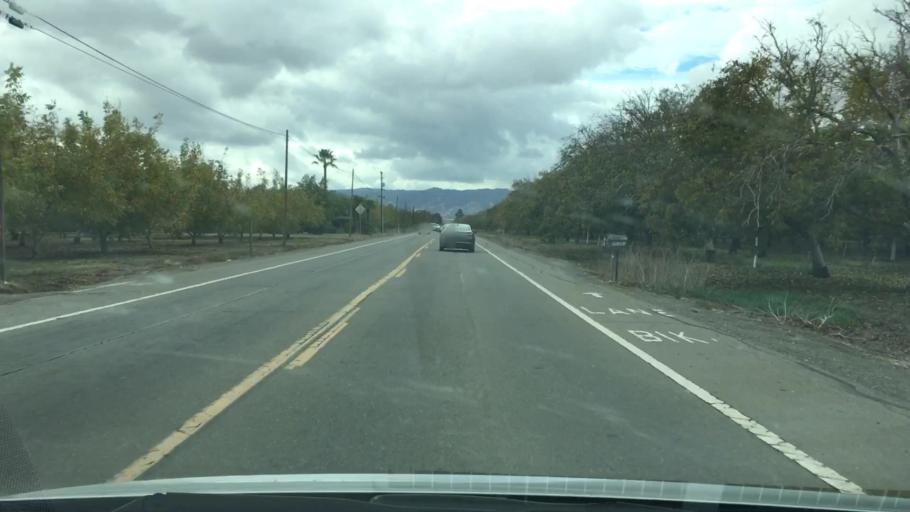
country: US
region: California
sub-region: Yolo County
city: Winters
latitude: 38.5398
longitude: -121.9297
